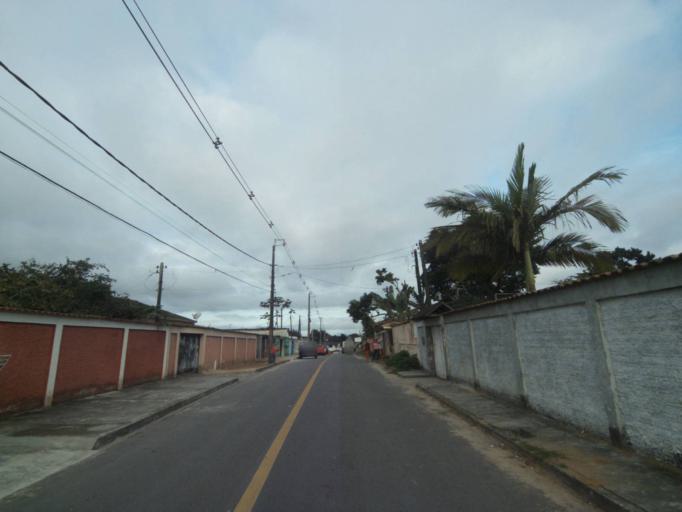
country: BR
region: Parana
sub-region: Paranagua
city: Paranagua
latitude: -25.5324
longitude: -48.5482
